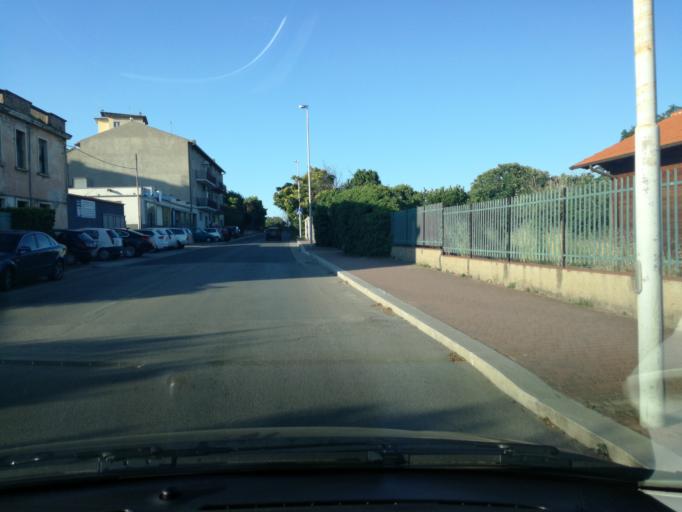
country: IT
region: Molise
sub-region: Provincia di Campobasso
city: Guglionesi
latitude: 41.9182
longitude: 14.9143
